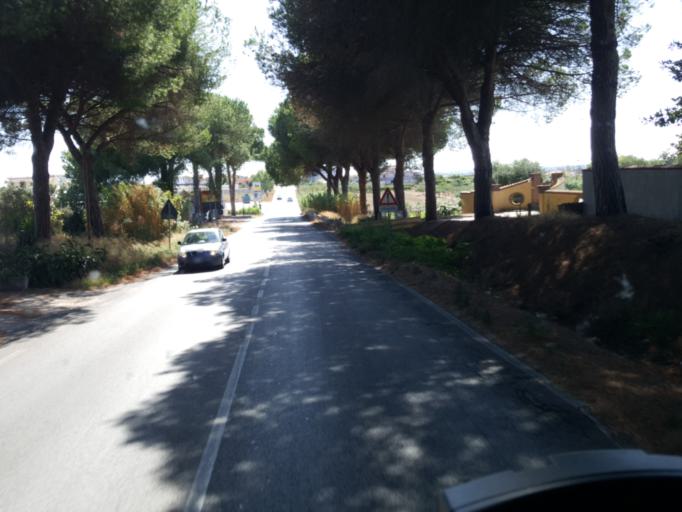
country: IT
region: Latium
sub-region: Citta metropolitana di Roma Capitale
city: Nettuno
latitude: 41.5084
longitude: 12.6911
